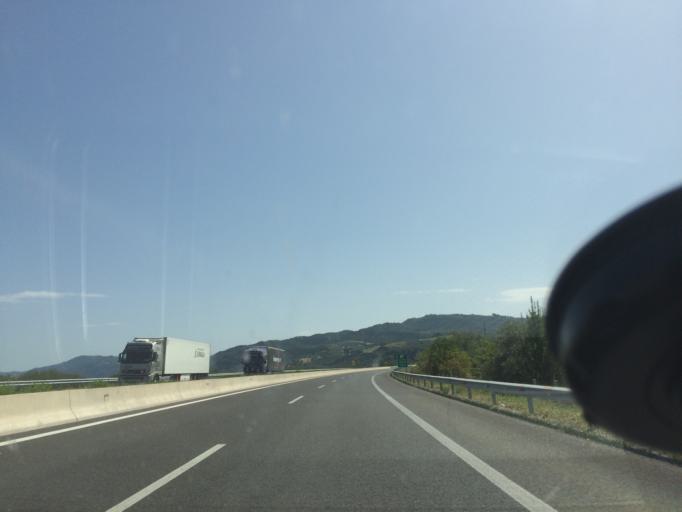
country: GR
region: Central Greece
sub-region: Nomos Fthiotidos
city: Molos
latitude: 38.8104
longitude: 22.6339
